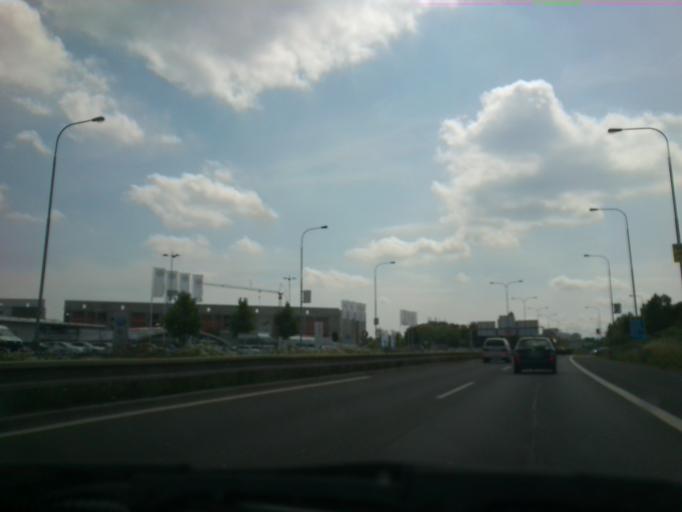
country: CZ
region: Praha
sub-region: Praha 9
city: Strizkov
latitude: 50.1334
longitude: 14.4910
